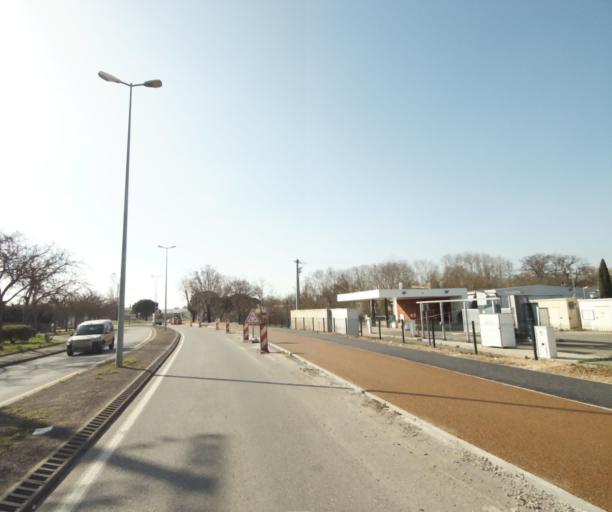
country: FR
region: Provence-Alpes-Cote d'Azur
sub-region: Departement des Bouches-du-Rhone
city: Aix-en-Provence
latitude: 43.5079
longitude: 5.4178
